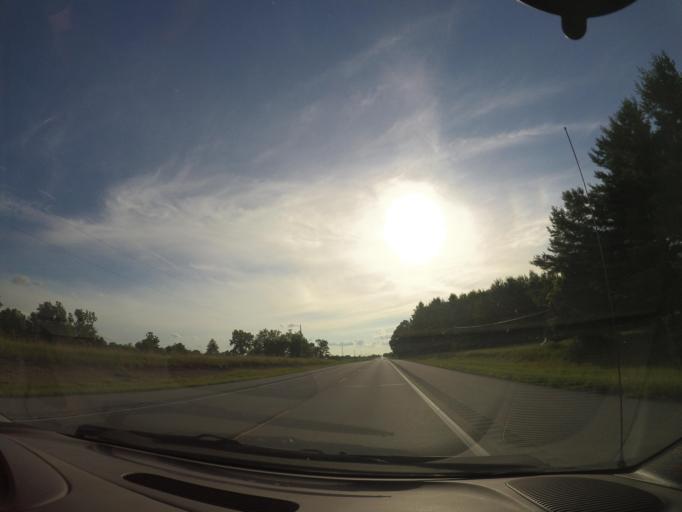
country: US
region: Ohio
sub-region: Williams County
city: Bryan
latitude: 41.4414
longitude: -84.6033
